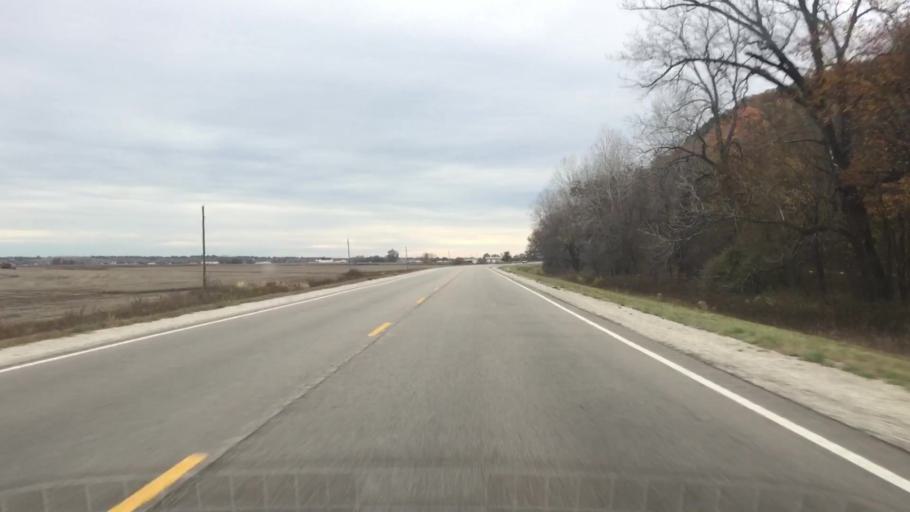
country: US
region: Missouri
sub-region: Cole County
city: Jefferson City
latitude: 38.5865
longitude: -92.1221
